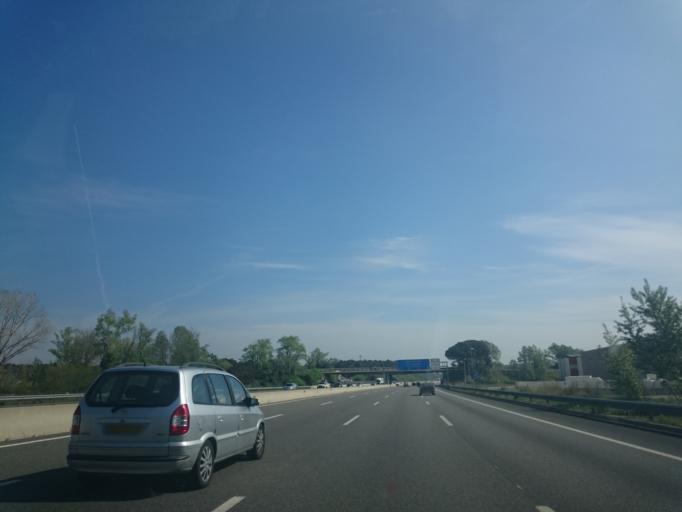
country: ES
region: Catalonia
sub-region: Provincia de Girona
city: Salt
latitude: 41.9887
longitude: 2.7869
